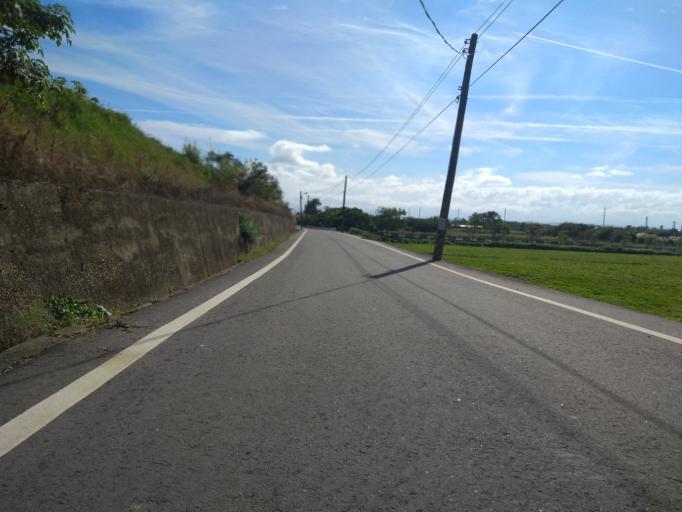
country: TW
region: Taiwan
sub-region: Hsinchu
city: Zhubei
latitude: 25.0002
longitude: 121.0389
